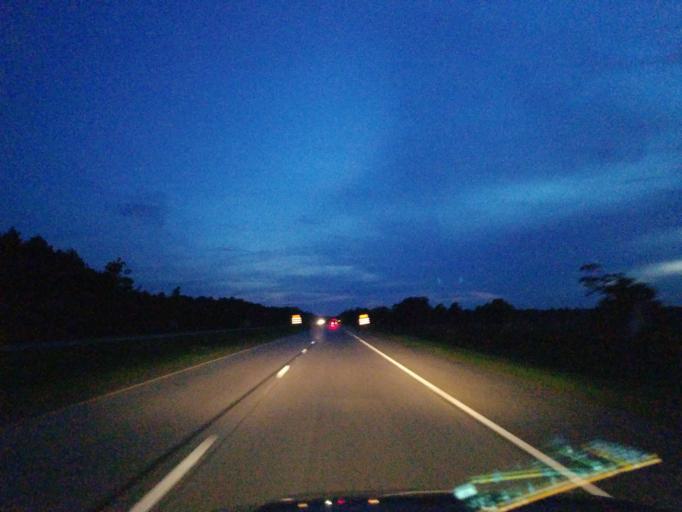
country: US
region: Mississippi
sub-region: Jones County
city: Ellisville
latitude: 31.5073
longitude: -89.2984
